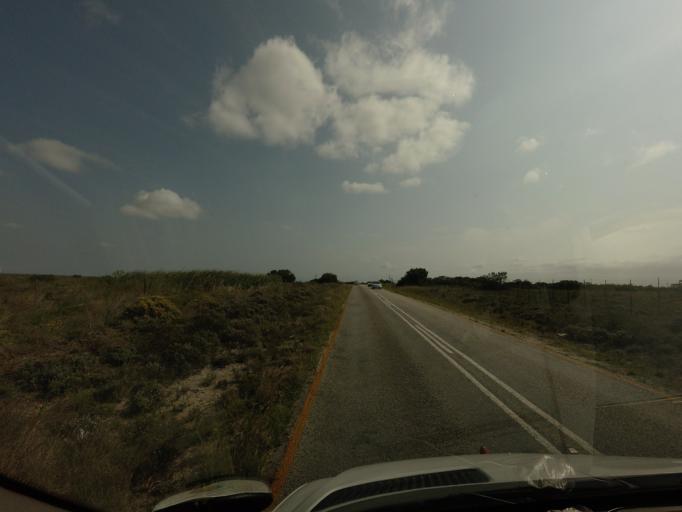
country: ZA
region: Eastern Cape
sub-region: Nelson Mandela Bay Metropolitan Municipality
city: Uitenhage
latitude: -33.7043
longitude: 25.5885
